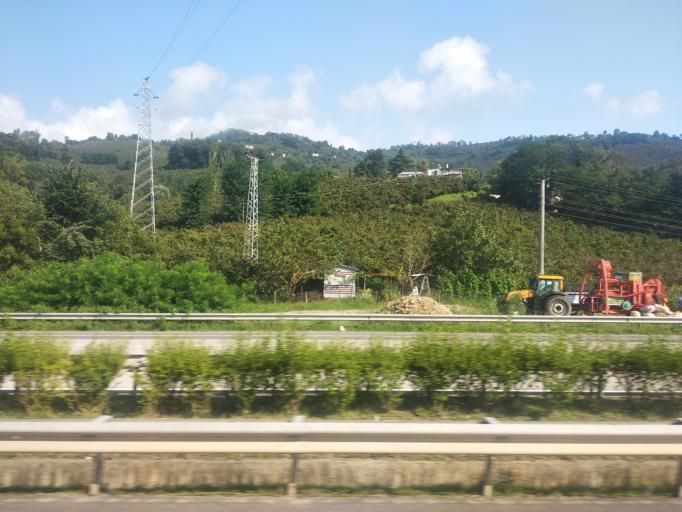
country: TR
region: Ordu
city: Ordu
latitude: 41.0087
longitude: 37.8305
